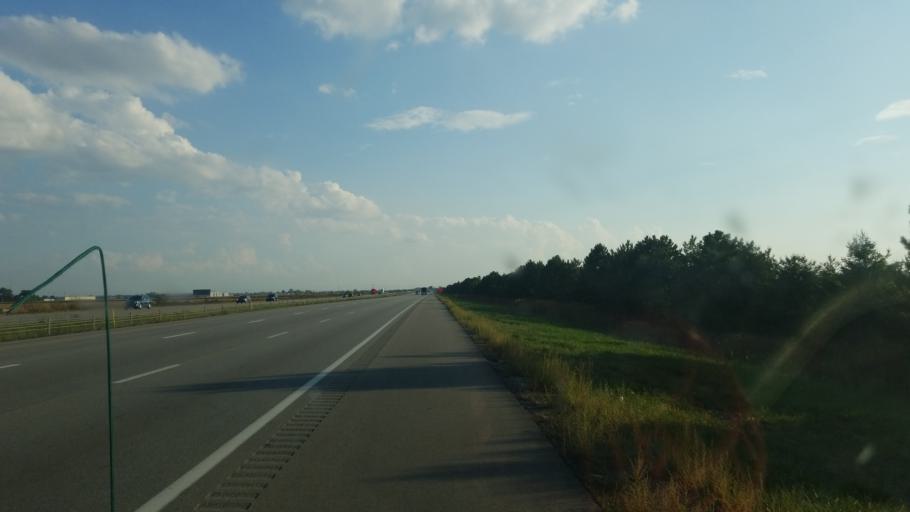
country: US
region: Ohio
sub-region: Wood County
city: Bowling Green
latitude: 41.4080
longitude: -83.6161
